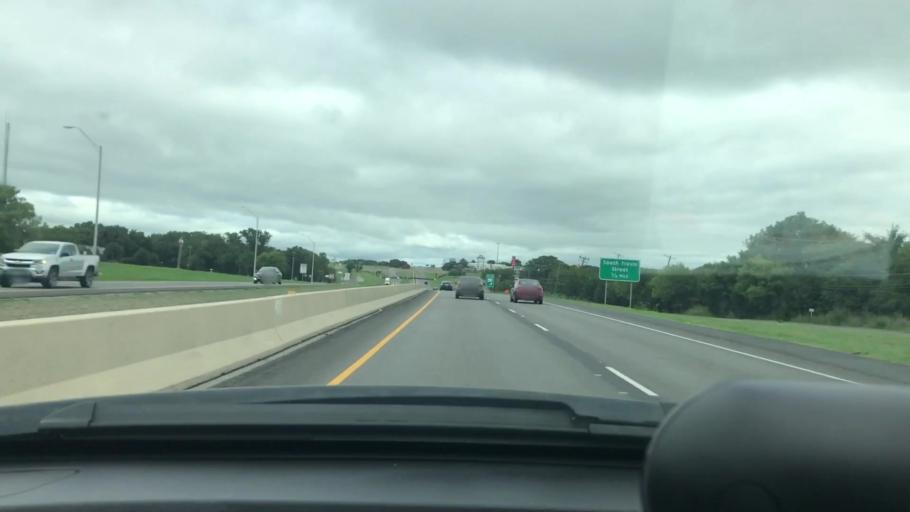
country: US
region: Texas
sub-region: Grayson County
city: Sherman
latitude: 33.5887
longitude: -96.6040
